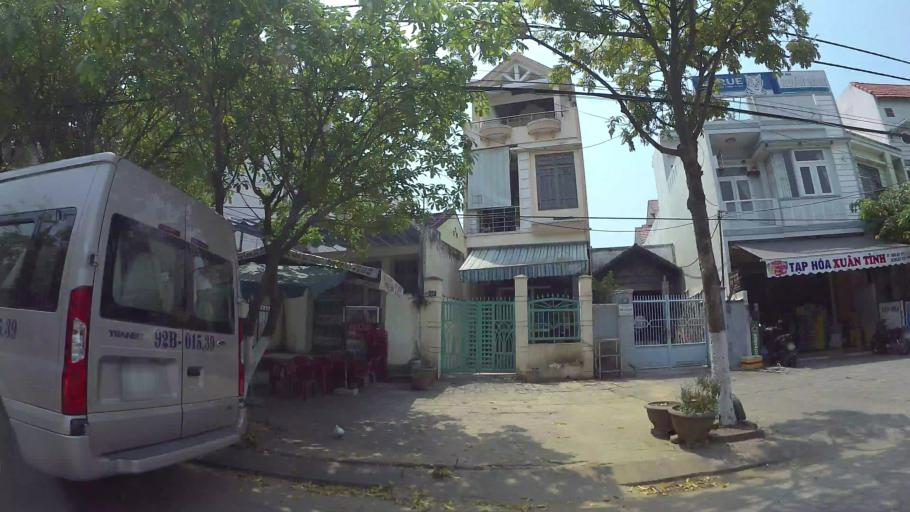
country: VN
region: Da Nang
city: Cam Le
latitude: 16.0215
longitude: 108.2144
